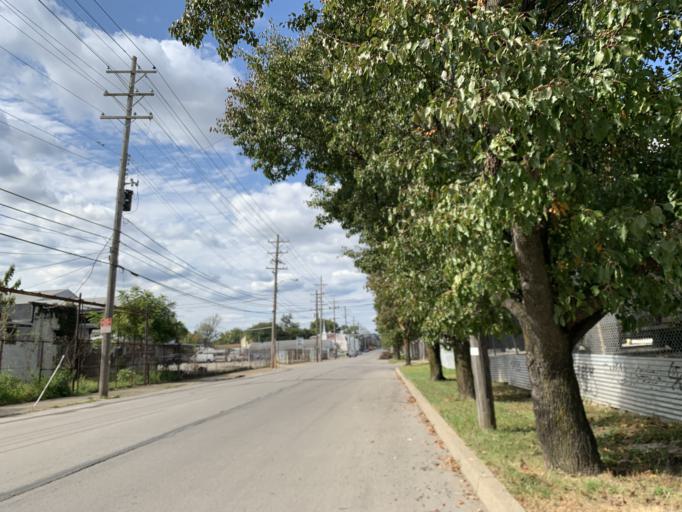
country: US
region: Kentucky
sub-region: Jefferson County
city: Louisville
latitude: 38.2625
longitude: -85.7745
